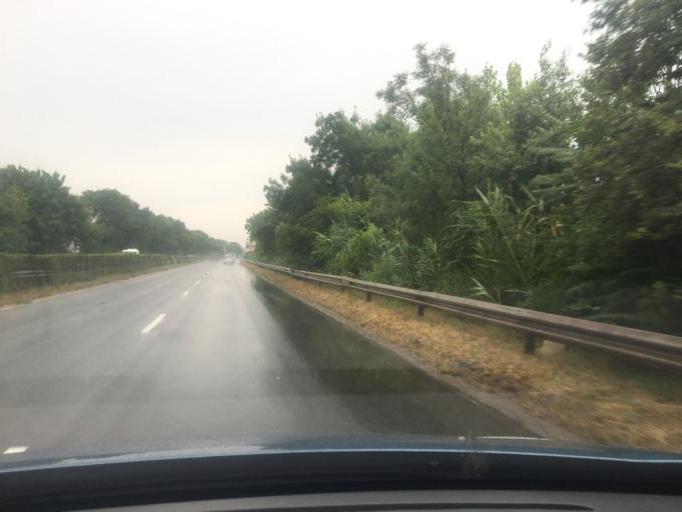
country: BG
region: Burgas
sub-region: Obshtina Burgas
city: Burgas
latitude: 42.5396
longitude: 27.4722
